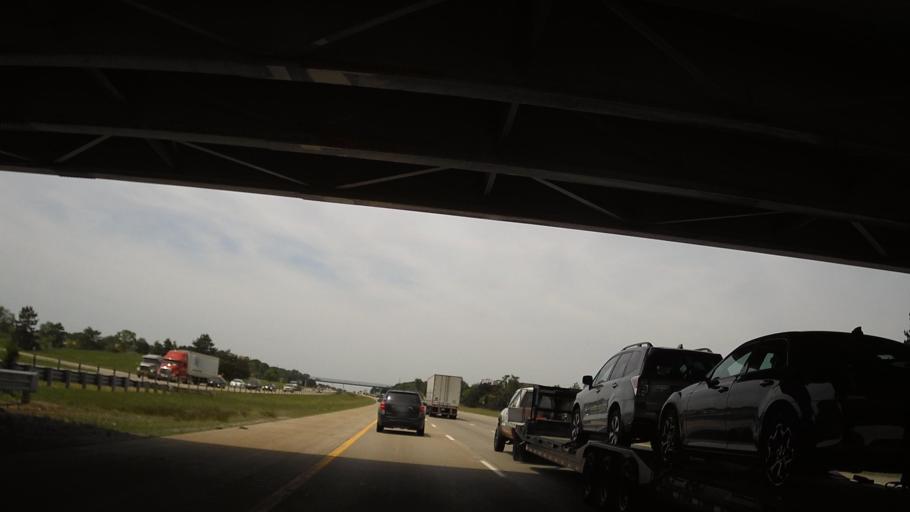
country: US
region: Michigan
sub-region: Wayne County
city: Belleville
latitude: 42.2200
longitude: -83.4850
